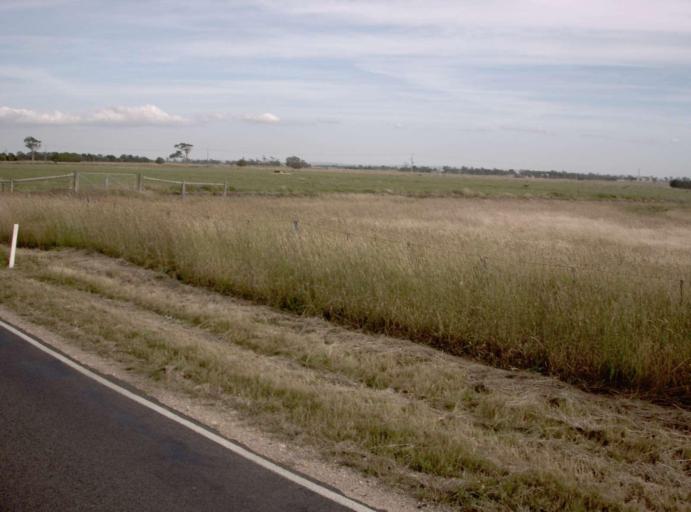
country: AU
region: Victoria
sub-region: Wellington
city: Heyfield
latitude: -38.0204
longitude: 146.7537
